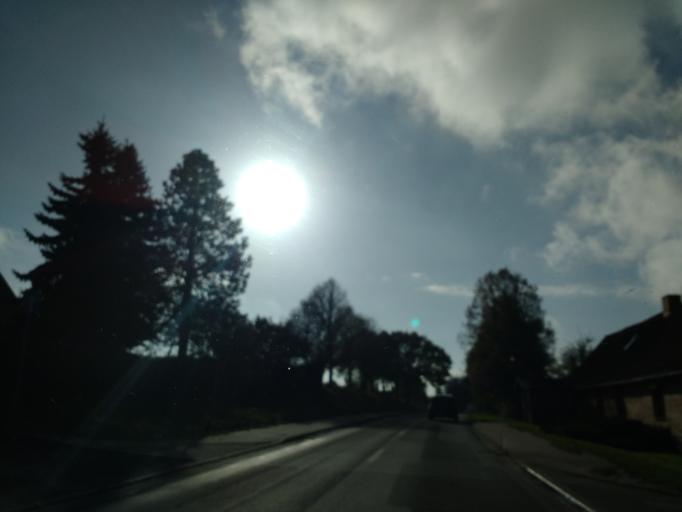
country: DE
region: Mecklenburg-Vorpommern
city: Klutz
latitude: 53.9549
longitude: 11.1640
